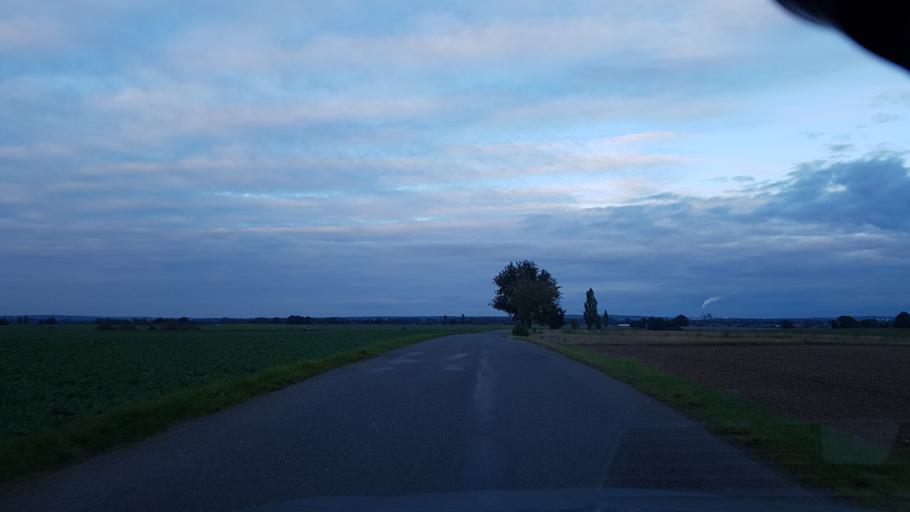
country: DE
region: Saxony
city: Ebersbach
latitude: 51.2622
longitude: 13.5953
